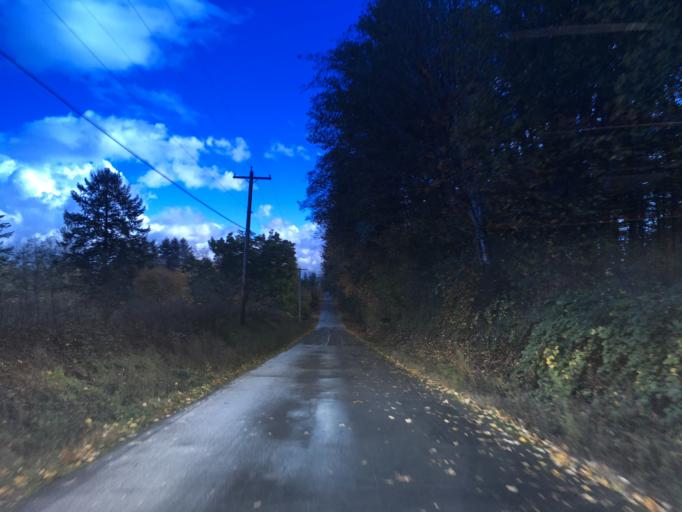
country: US
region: Oregon
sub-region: Multnomah County
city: Troutdale
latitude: 45.5045
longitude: -122.3721
